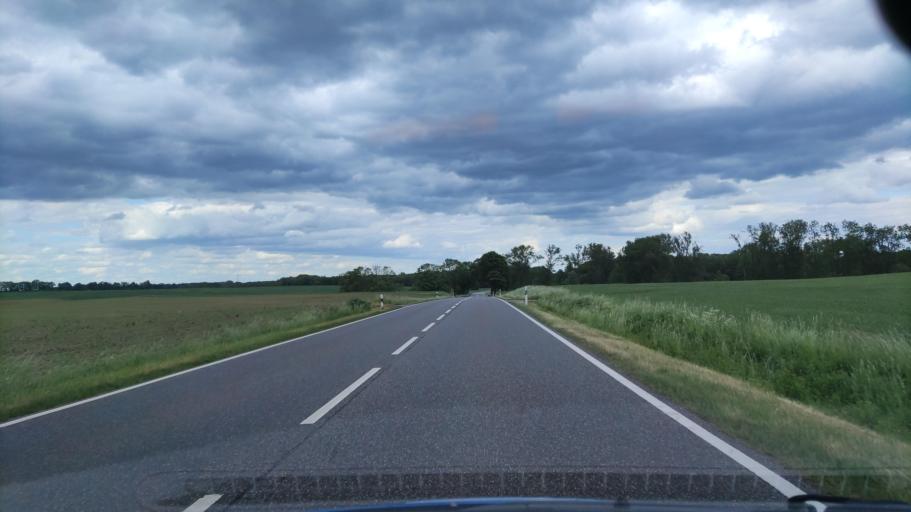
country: DE
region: Mecklenburg-Vorpommern
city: Neuburg
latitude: 53.4461
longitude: 11.9218
